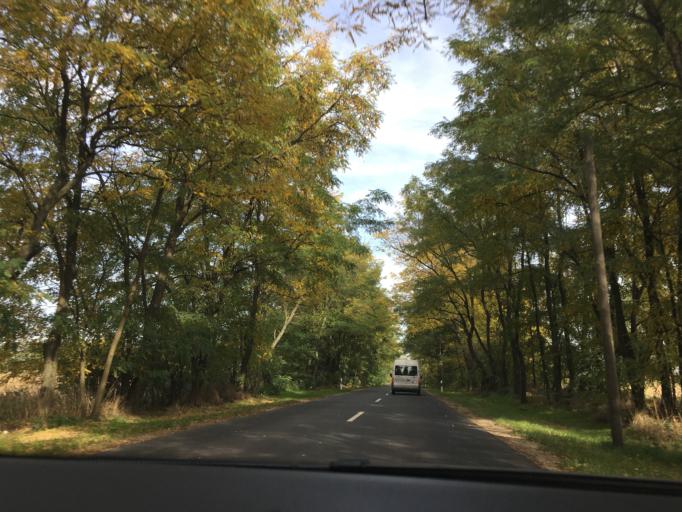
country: HU
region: Szabolcs-Szatmar-Bereg
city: Nagykallo
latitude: 47.8499
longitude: 21.7882
